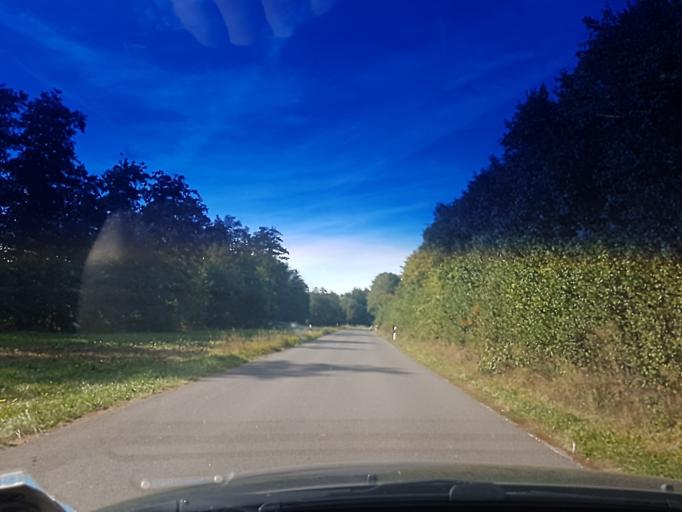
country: DE
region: Bavaria
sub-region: Upper Franconia
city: Schlusselfeld
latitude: 49.7696
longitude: 10.6097
